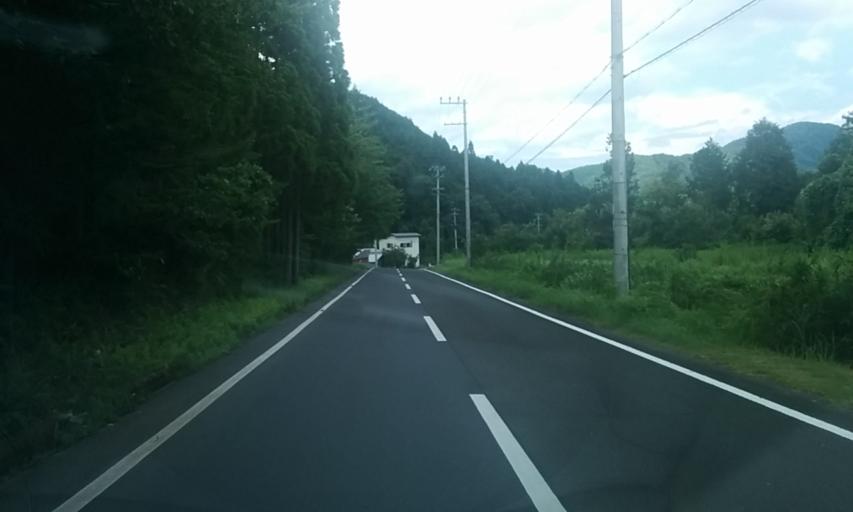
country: JP
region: Kyoto
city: Ayabe
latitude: 35.2889
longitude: 135.3286
